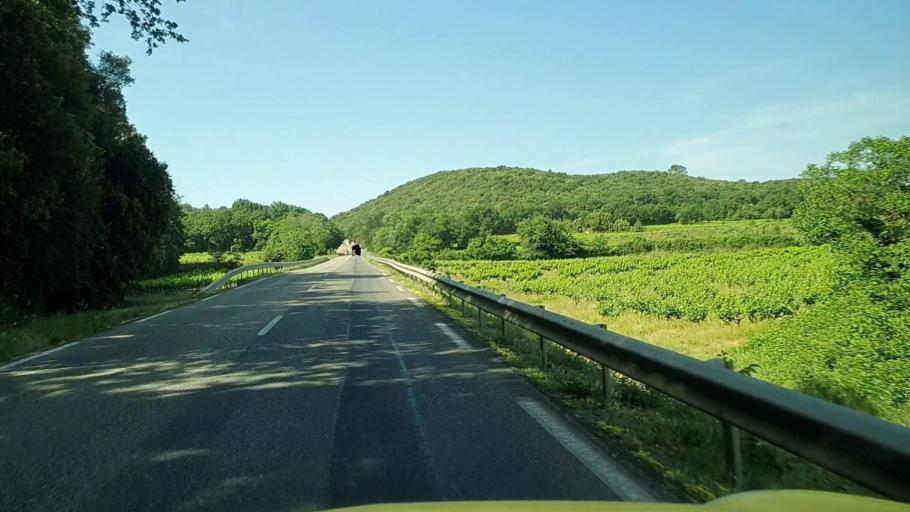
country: FR
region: Languedoc-Roussillon
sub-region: Departement du Gard
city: Connaux
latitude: 44.0749
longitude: 4.5841
